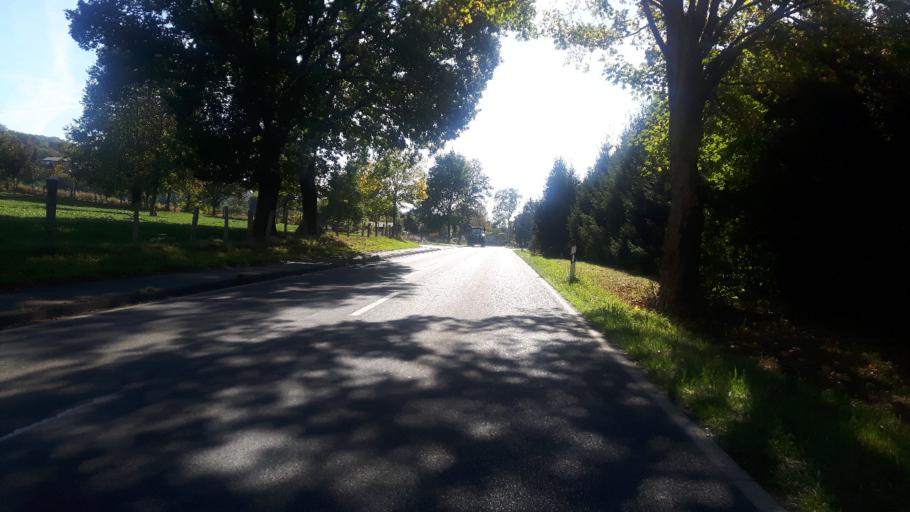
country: DE
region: Rheinland-Pfalz
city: Niederirsen
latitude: 50.7865
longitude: 7.6233
